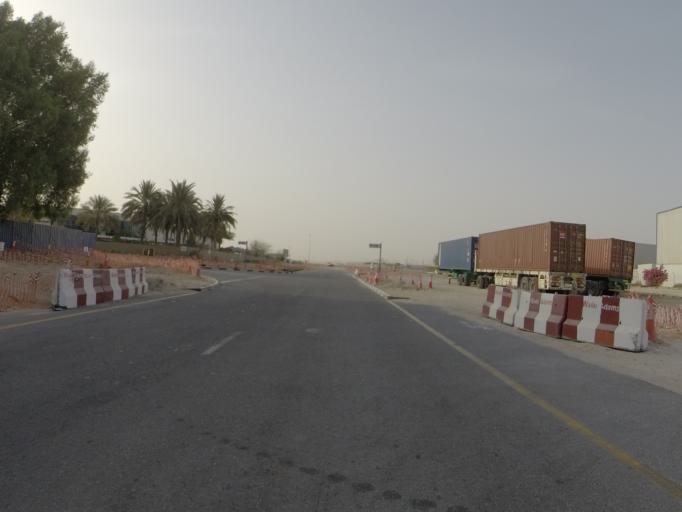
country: AE
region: Dubai
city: Dubai
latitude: 24.9524
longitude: 55.0668
